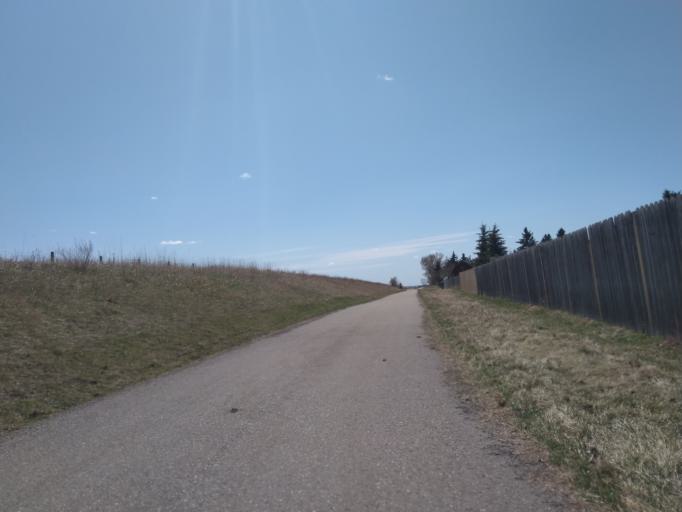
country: CA
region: Alberta
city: Chestermere
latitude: 51.0639
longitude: -113.9235
